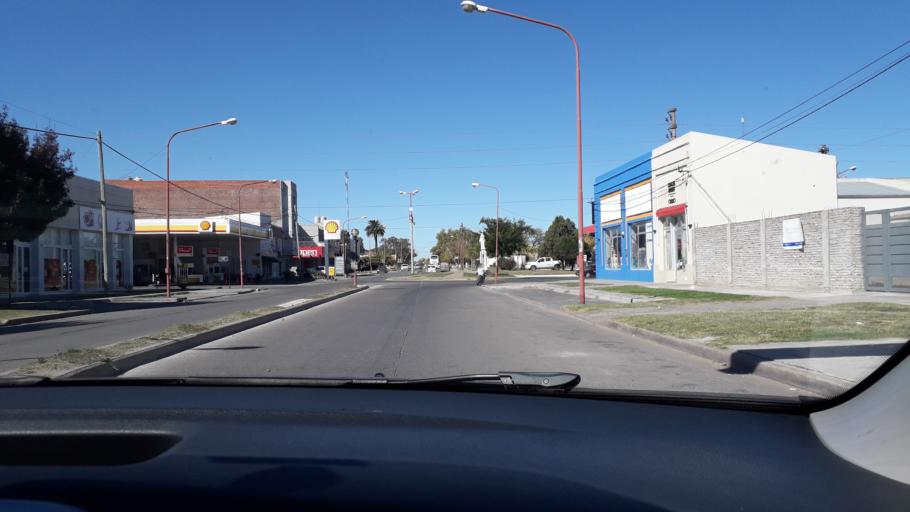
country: AR
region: Buenos Aires
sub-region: Partido de Azul
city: Azul
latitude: -36.7829
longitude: -59.8522
